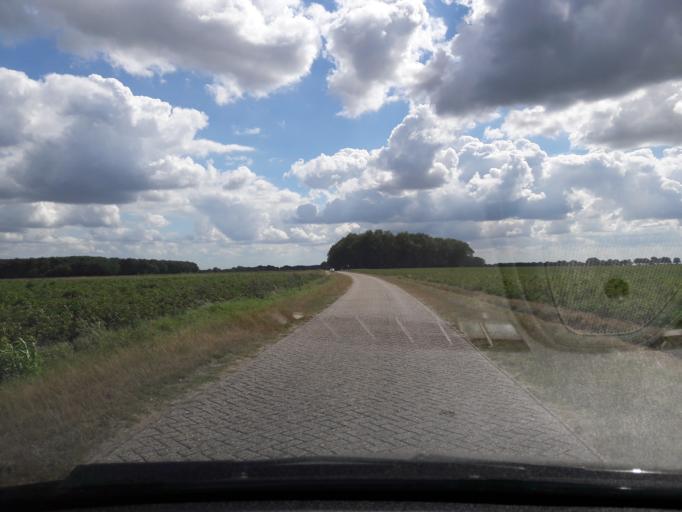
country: NL
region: Drenthe
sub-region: Gemeente Borger-Odoorn
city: Borger
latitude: 52.9460
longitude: 6.7972
